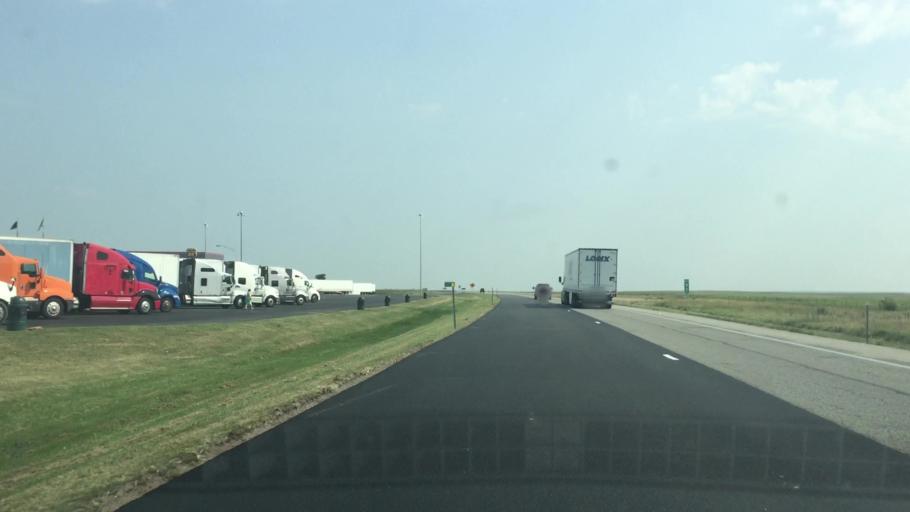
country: US
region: Kansas
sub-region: Chase County
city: Cottonwood Falls
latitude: 38.0945
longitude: -96.5791
